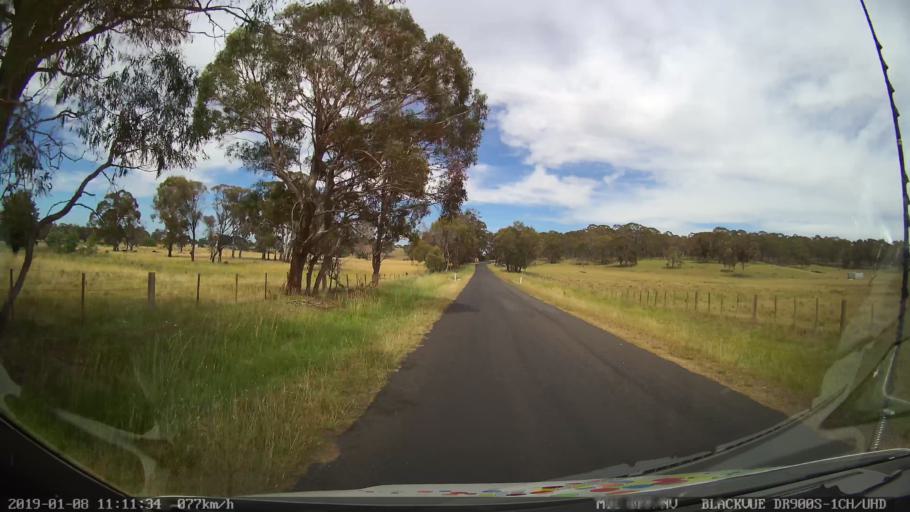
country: AU
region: New South Wales
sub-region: Guyra
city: Guyra
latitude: -30.2265
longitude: 151.6224
